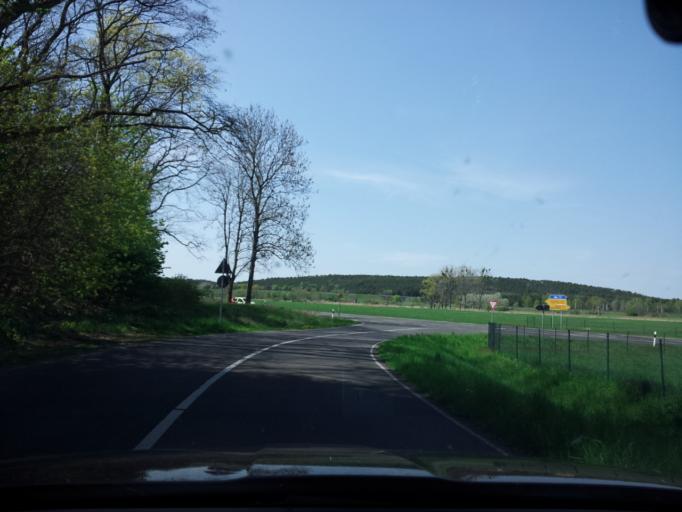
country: DE
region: Brandenburg
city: Michendorf
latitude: 52.3182
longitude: 13.1130
